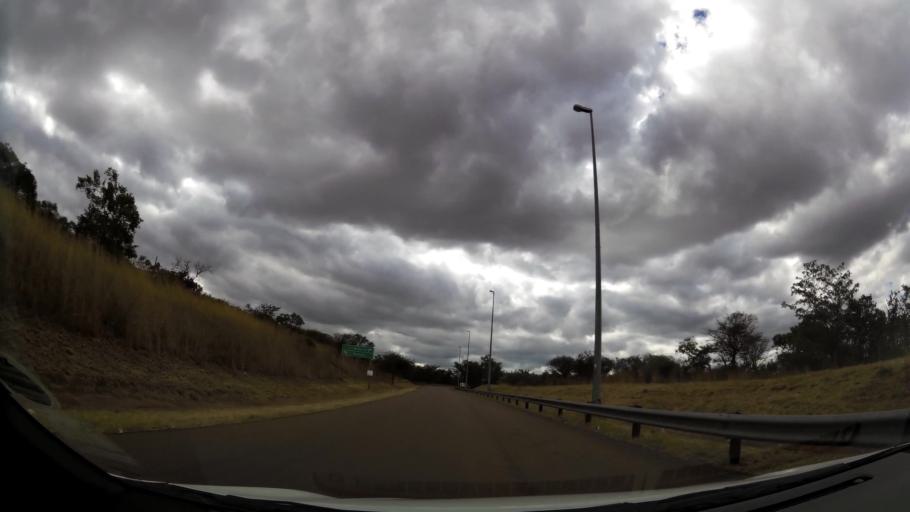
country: ZA
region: Limpopo
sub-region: Waterberg District Municipality
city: Modimolle
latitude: -24.7794
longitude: 28.4722
